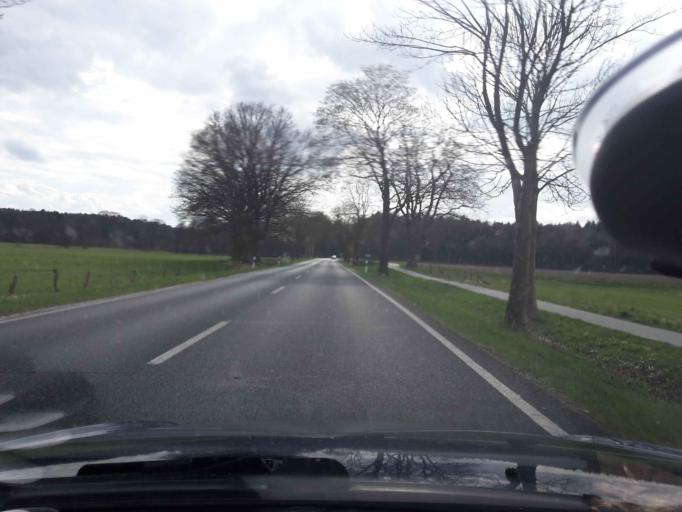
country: DE
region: Lower Saxony
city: Jesteburg
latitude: 53.2970
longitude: 9.9289
